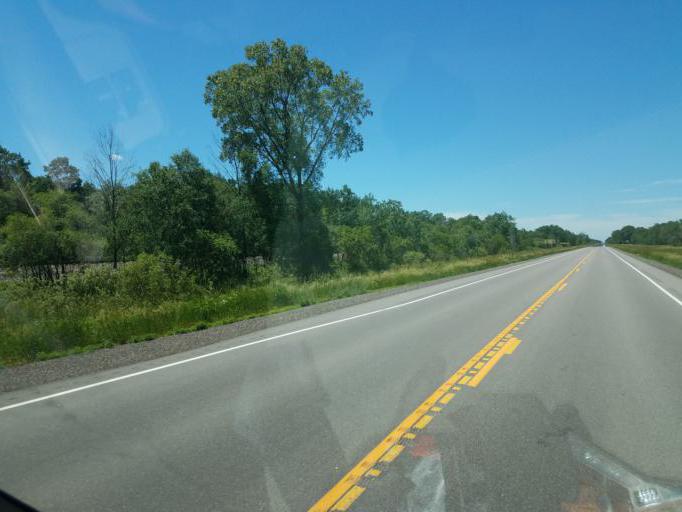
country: US
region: Wisconsin
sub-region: Juneau County
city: New Lisbon
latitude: 44.0250
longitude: -90.1574
